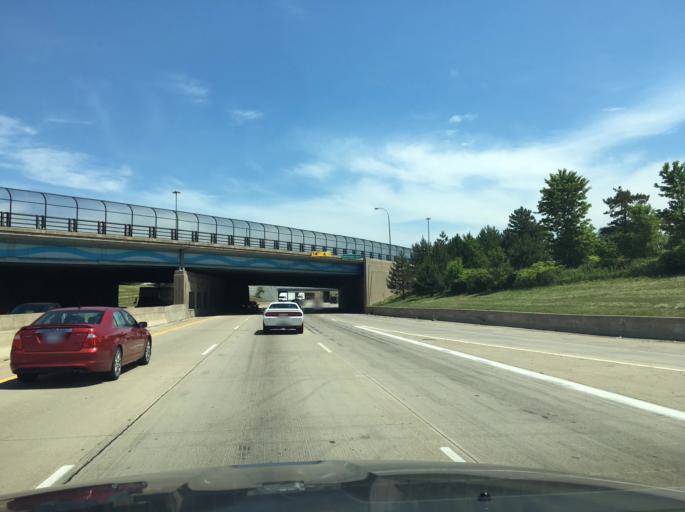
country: US
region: Michigan
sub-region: Wayne County
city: Dearborn
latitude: 42.3256
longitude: -83.1613
